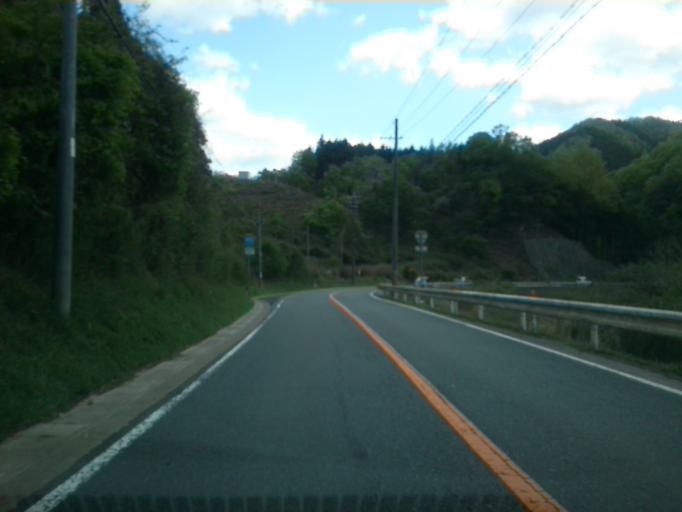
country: JP
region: Kyoto
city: Fukuchiyama
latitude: 35.3437
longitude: 135.0666
